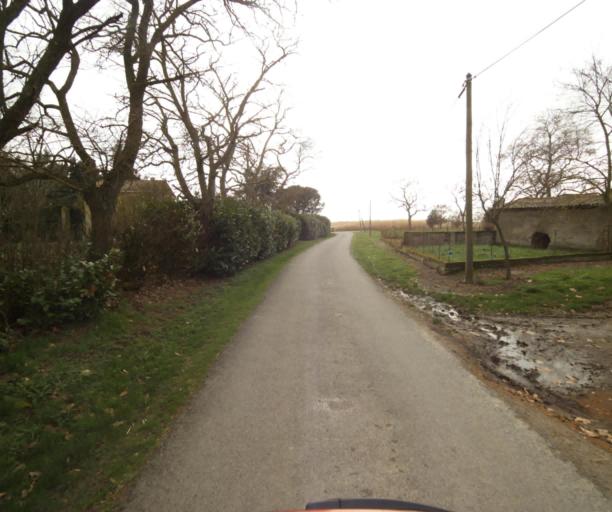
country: FR
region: Midi-Pyrenees
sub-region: Departement de l'Ariege
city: Mazeres
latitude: 43.1951
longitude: 1.6702
